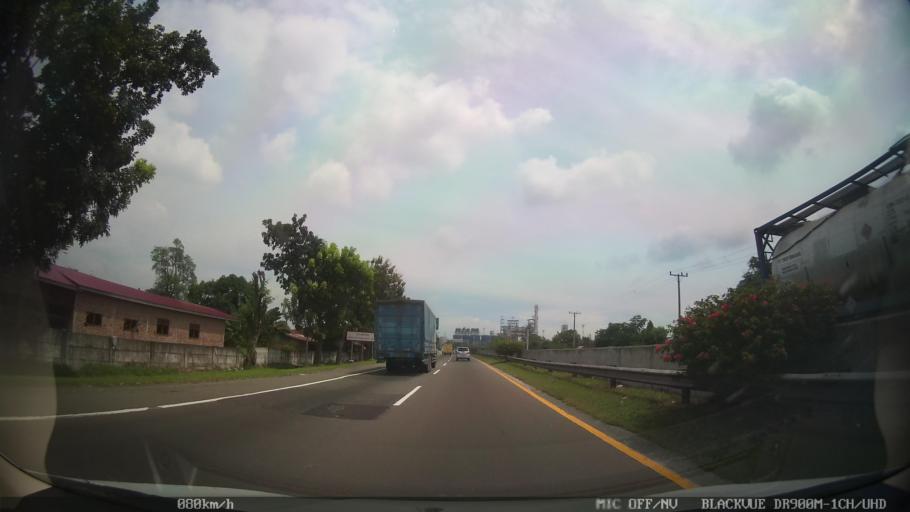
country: ID
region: North Sumatra
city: Labuhan Deli
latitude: 3.6565
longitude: 98.6826
